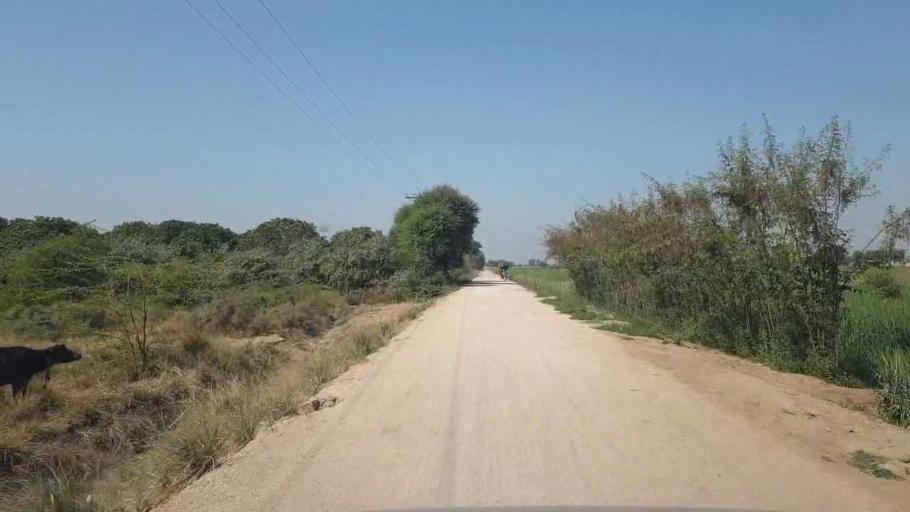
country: PK
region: Sindh
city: Digri
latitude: 25.2551
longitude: 69.2265
